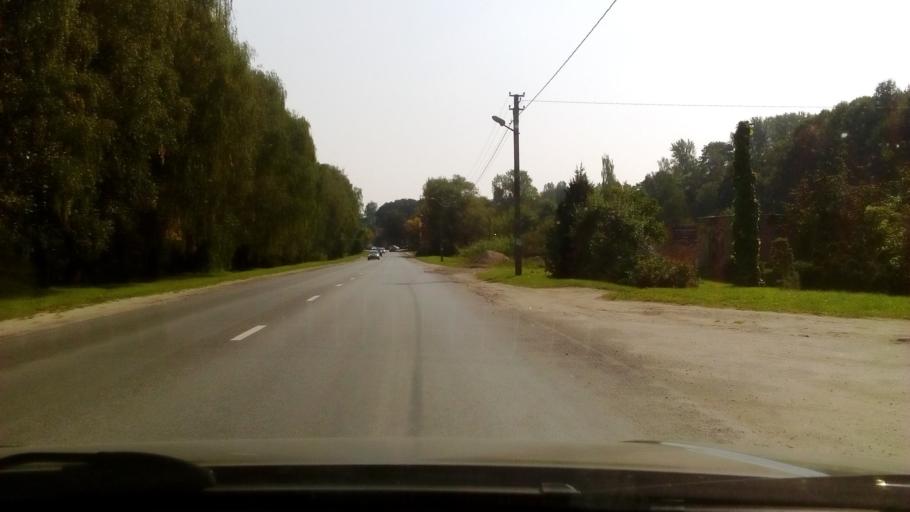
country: LT
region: Alytaus apskritis
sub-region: Alytus
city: Alytus
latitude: 54.4052
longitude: 24.0348
